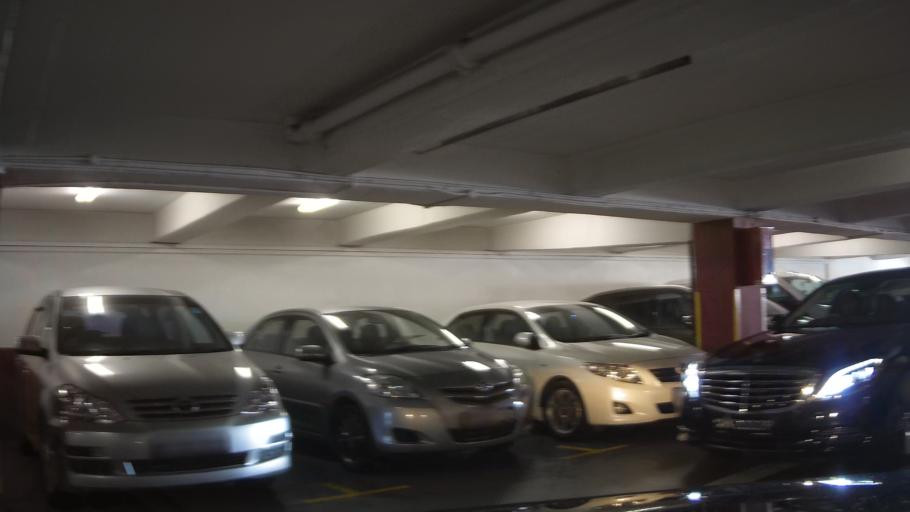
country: SG
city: Singapore
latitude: 1.2975
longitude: 103.8316
